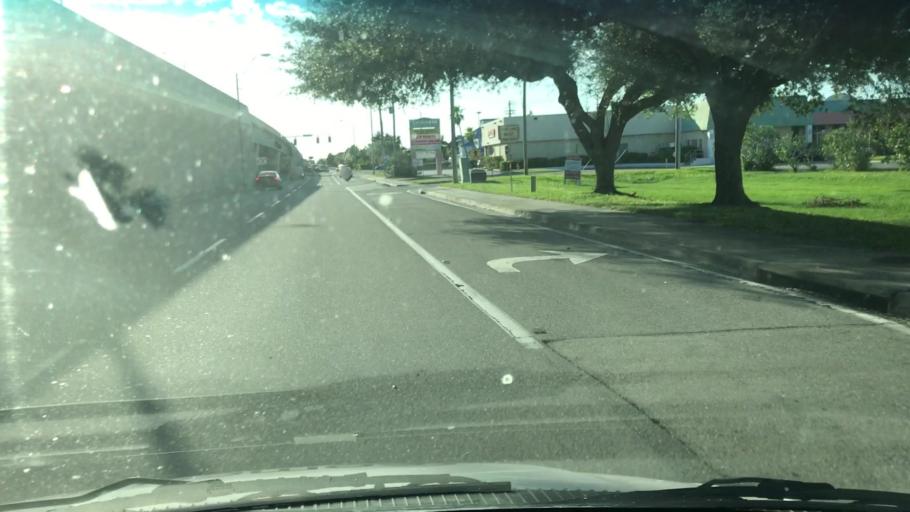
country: US
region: Florida
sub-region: Lee County
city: Cape Coral
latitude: 26.6077
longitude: -81.9395
